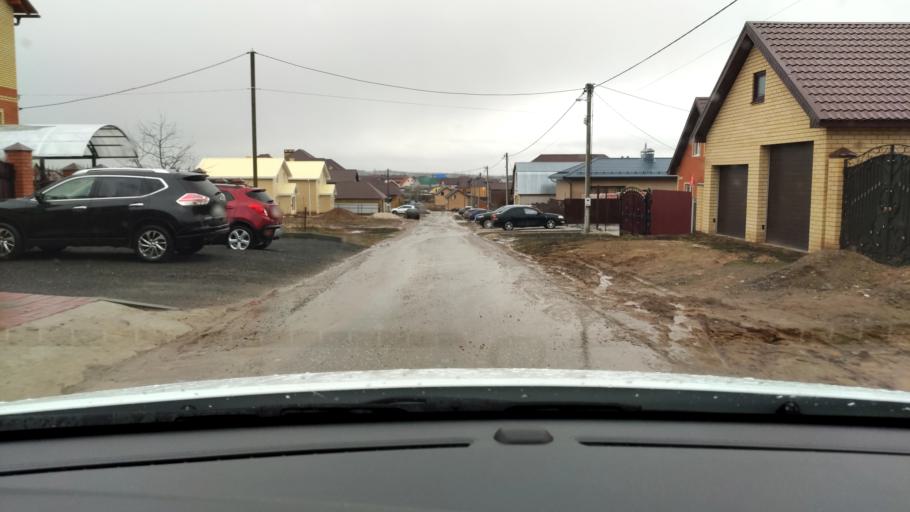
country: RU
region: Tatarstan
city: Vysokaya Gora
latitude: 55.9020
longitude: 49.3177
